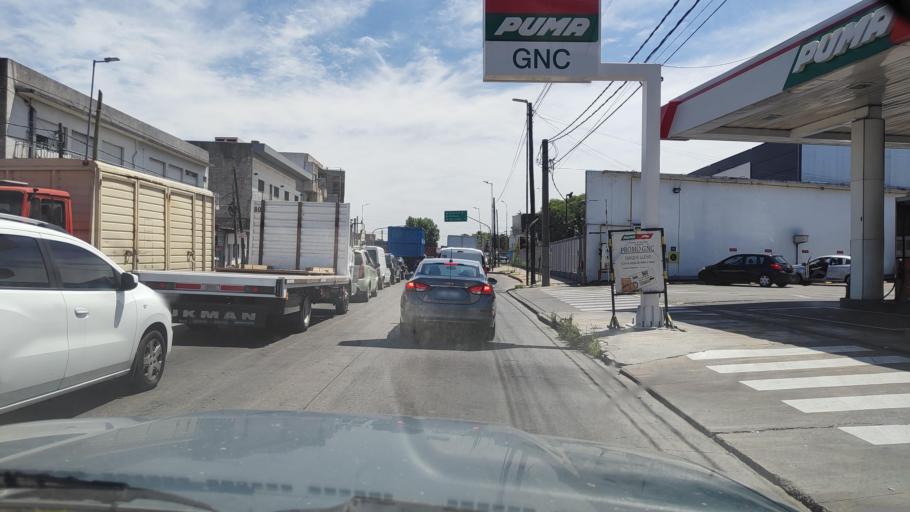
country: AR
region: Buenos Aires
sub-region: Partido de Moron
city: Moron
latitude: -34.6420
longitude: -58.6249
